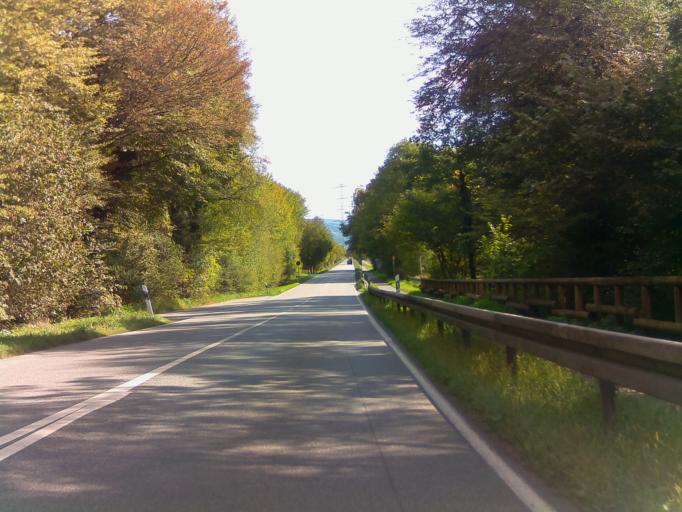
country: DE
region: Hesse
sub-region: Regierungsbezirk Darmstadt
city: Alsbach-Hahnlein
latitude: 49.7426
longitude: 8.5465
